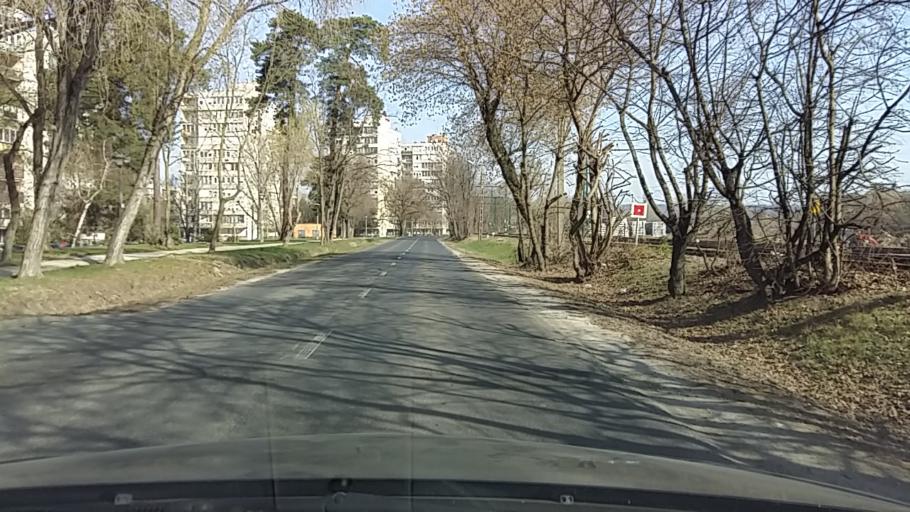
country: HU
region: Pest
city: Godollo
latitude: 47.5946
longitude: 19.3572
